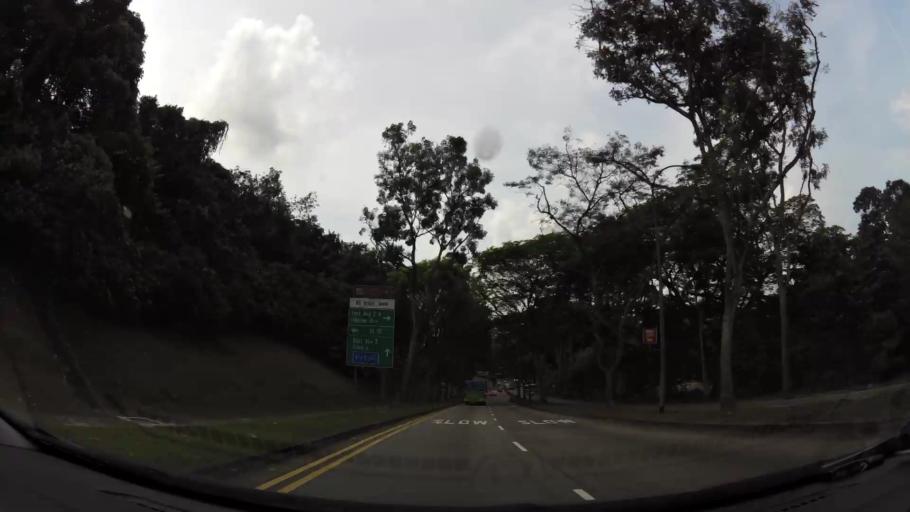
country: SG
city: Singapore
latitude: 1.3466
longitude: 103.7623
